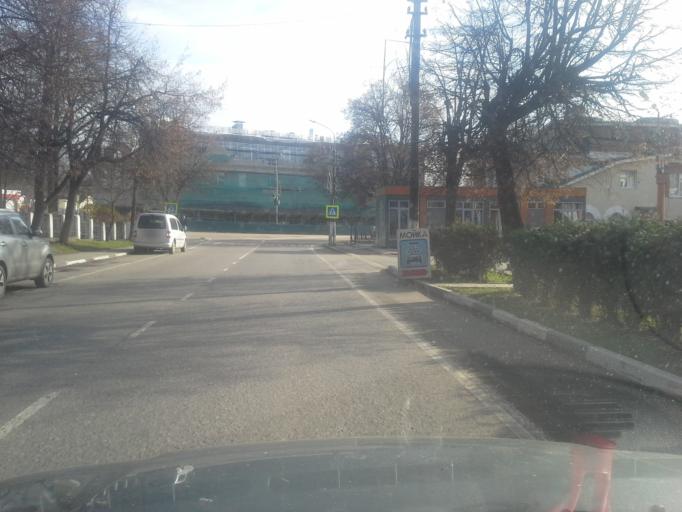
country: RU
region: Moskovskaya
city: Zvenigorod
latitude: 55.7290
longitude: 36.8595
